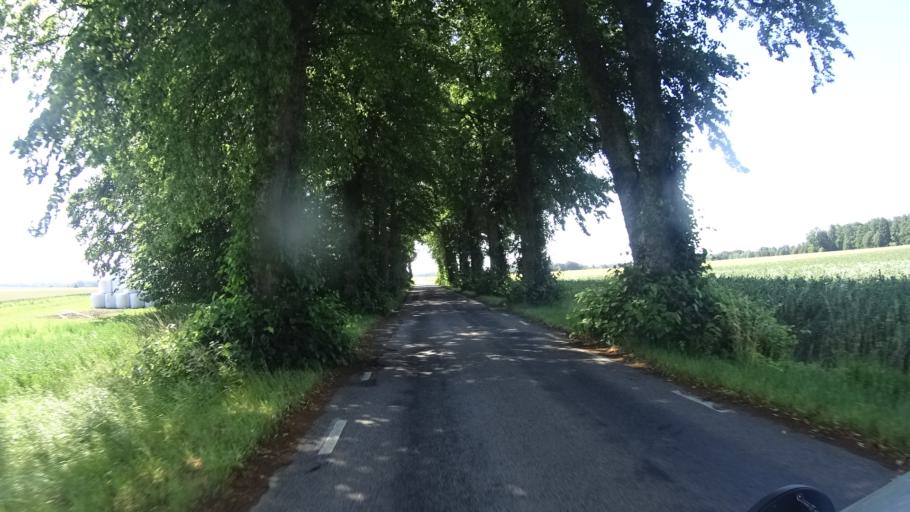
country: SE
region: OEstergoetland
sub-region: Vadstena Kommun
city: Herrestad
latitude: 58.3178
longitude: 14.8425
